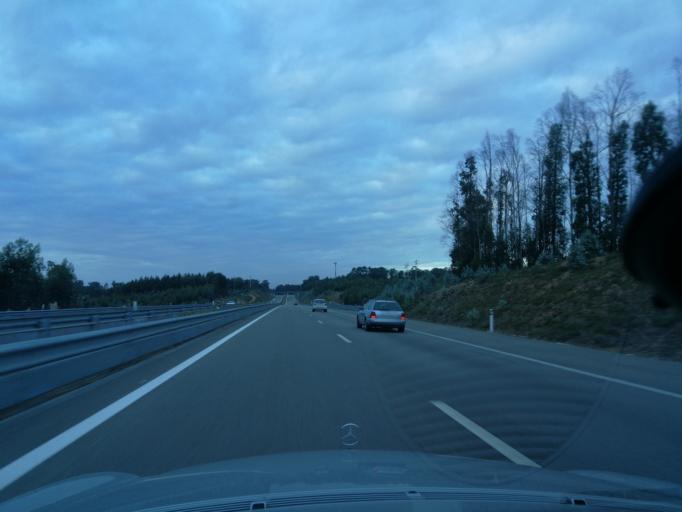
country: PT
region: Aveiro
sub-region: Estarreja
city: Salreu
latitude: 40.7115
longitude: -8.5328
